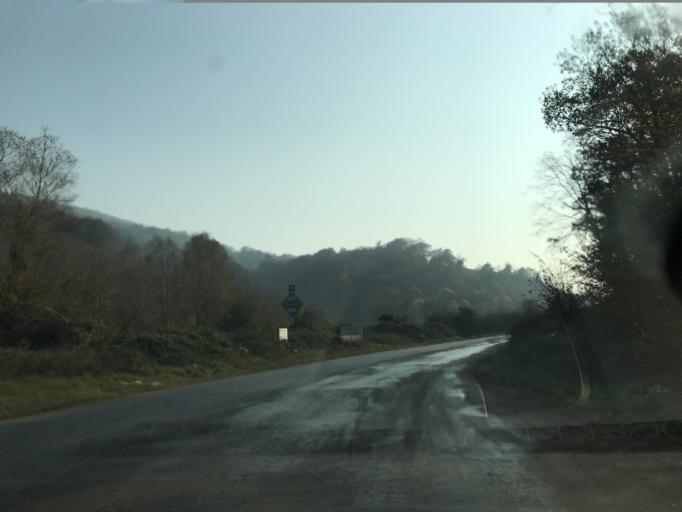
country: TR
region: Duzce
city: Cumayeri
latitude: 40.8942
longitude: 30.9565
